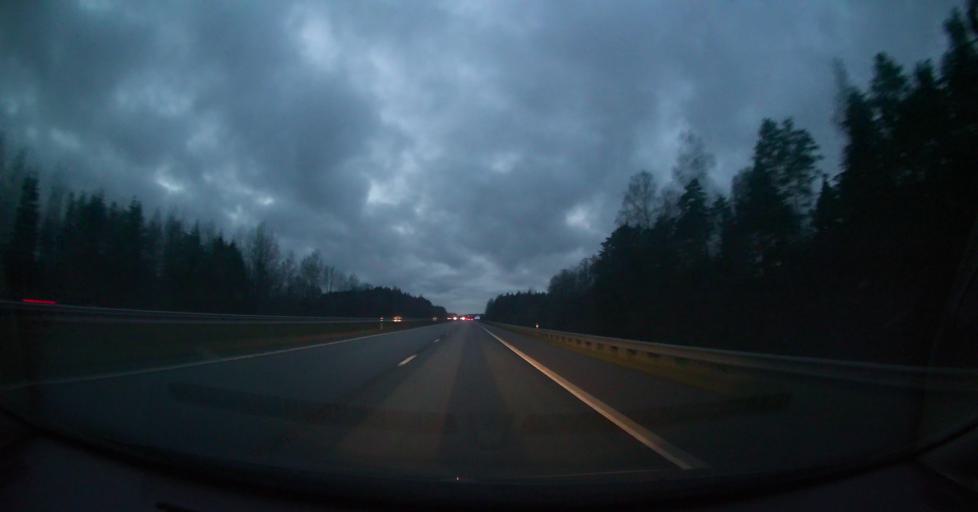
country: EE
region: Harju
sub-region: Kuusalu vald
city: Kuusalu
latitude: 59.4588
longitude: 25.5468
